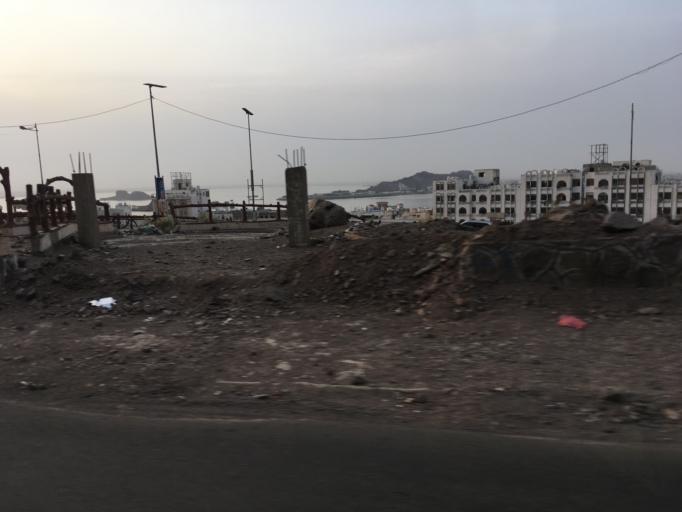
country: YE
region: Aden
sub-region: Craiter
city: Crater
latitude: 12.7888
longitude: 45.0215
